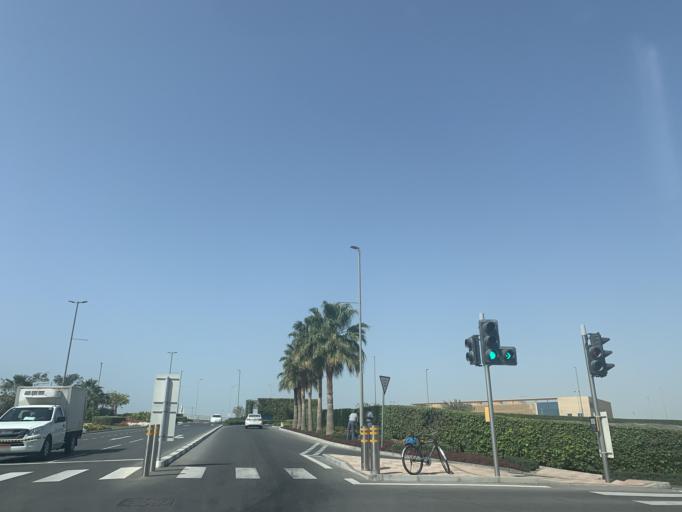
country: BH
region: Muharraq
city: Al Muharraq
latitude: 26.2510
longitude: 50.5818
